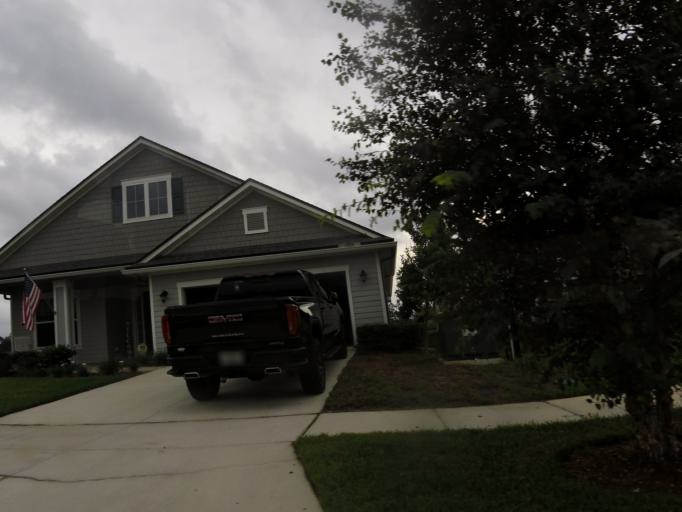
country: US
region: Florida
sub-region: Clay County
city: Middleburg
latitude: 30.1101
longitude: -81.8627
